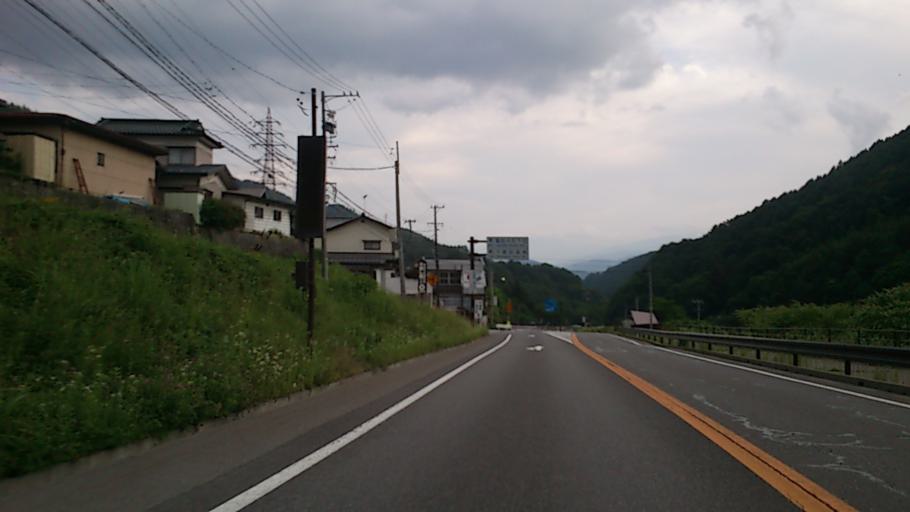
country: JP
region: Nagano
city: Suwa
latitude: 36.1059
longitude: 138.0957
